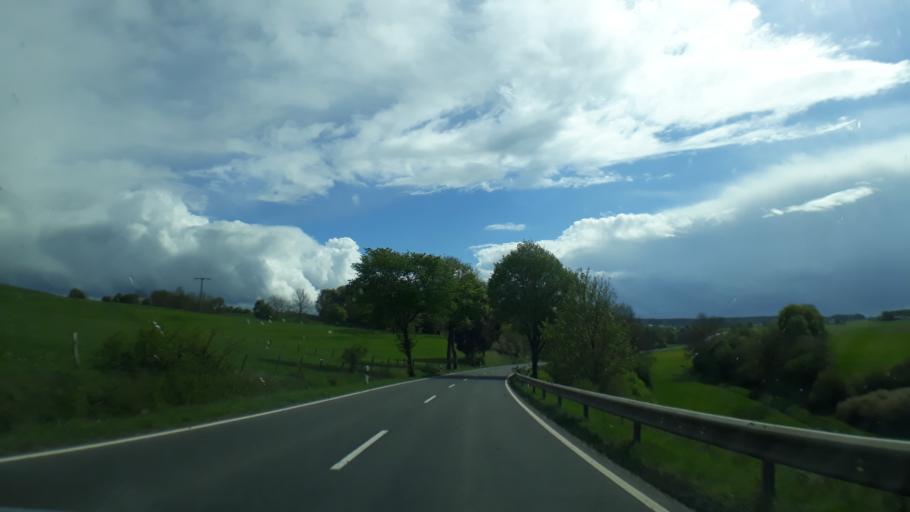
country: DE
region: North Rhine-Westphalia
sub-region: Regierungsbezirk Koln
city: Kall
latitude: 50.5063
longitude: 6.5370
